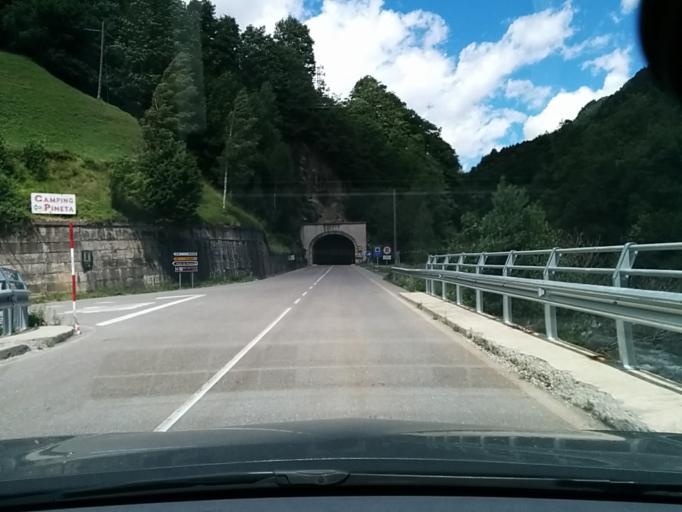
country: ES
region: Aragon
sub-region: Provincia de Huesca
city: Bielsa
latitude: 42.6386
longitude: 0.2154
